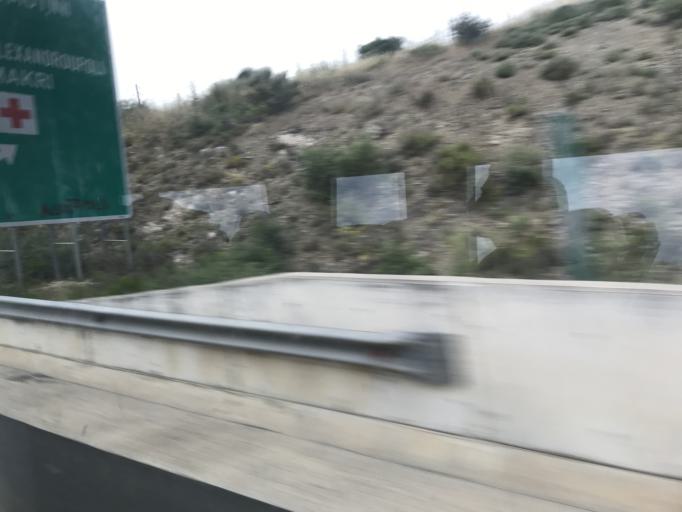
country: GR
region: East Macedonia and Thrace
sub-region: Nomos Evrou
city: Alexandroupoli
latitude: 40.8599
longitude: 25.7532
